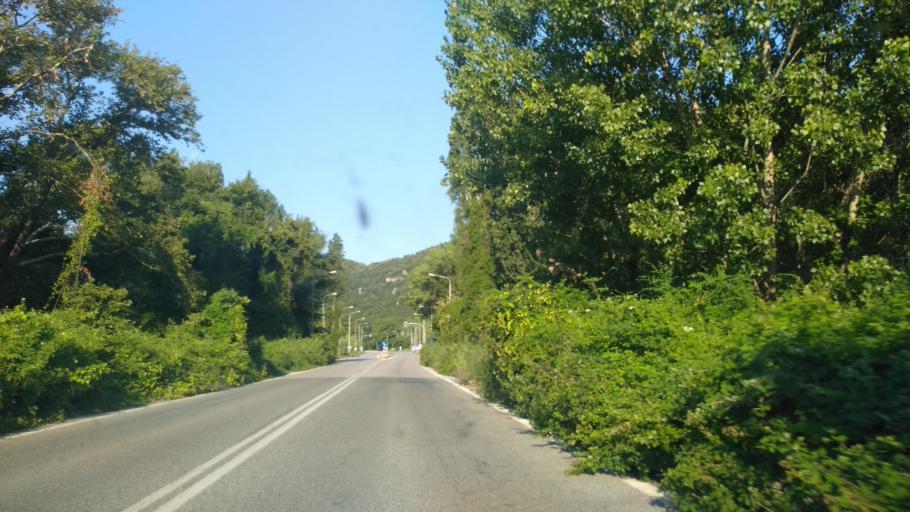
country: GR
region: Central Macedonia
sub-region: Nomos Thessalonikis
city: Stavros
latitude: 40.6729
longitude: 23.6664
